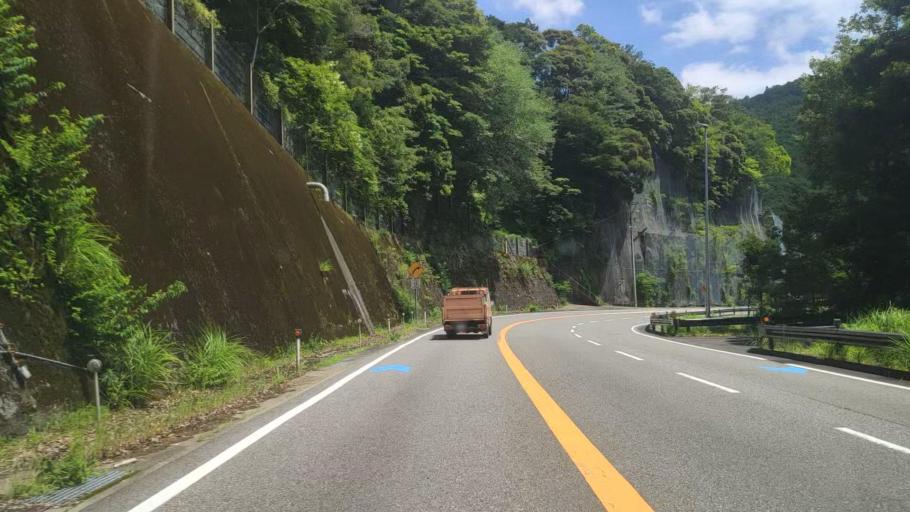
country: JP
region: Mie
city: Owase
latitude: 33.9198
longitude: 136.1026
